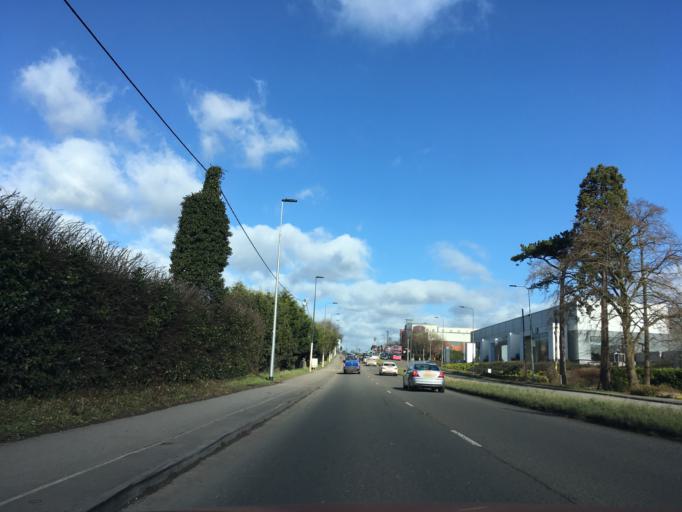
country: GB
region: England
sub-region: South Gloucestershire
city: Almondsbury
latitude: 51.5214
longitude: -2.6193
